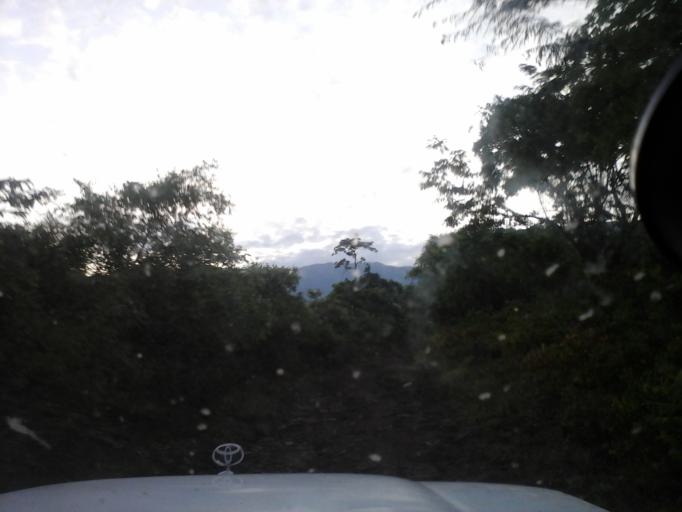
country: CO
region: Cesar
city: Agustin Codazzi
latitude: 10.1730
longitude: -73.1556
